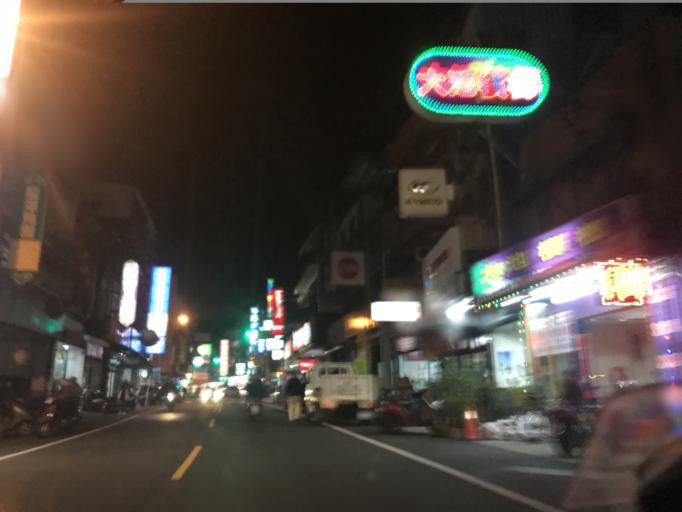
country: TW
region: Taiwan
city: Daxi
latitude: 24.8667
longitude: 121.2136
